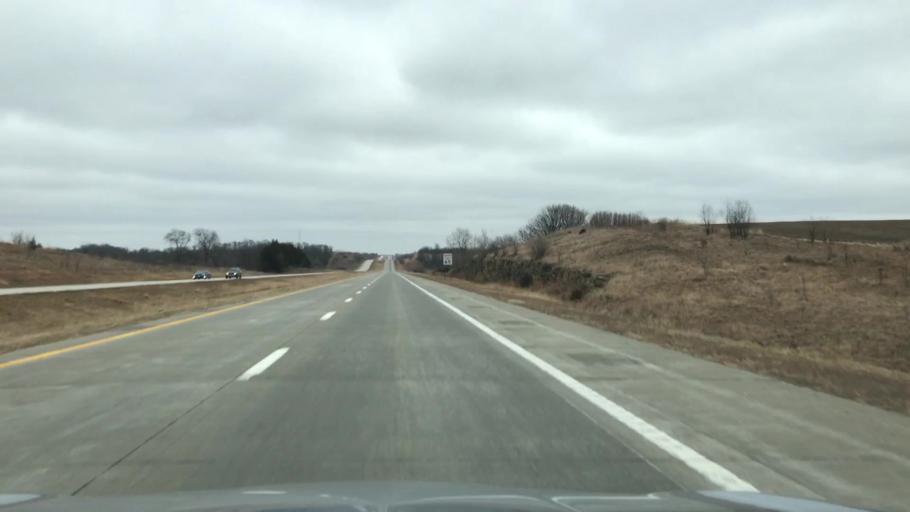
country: US
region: Missouri
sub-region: Caldwell County
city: Hamilton
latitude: 39.7350
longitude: -93.8318
